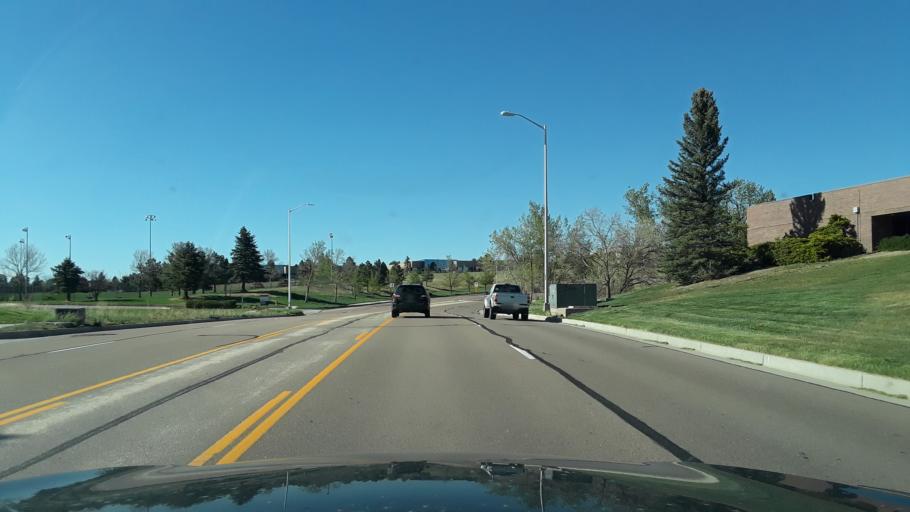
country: US
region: Colorado
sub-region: El Paso County
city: Air Force Academy
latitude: 38.9542
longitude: -104.7920
